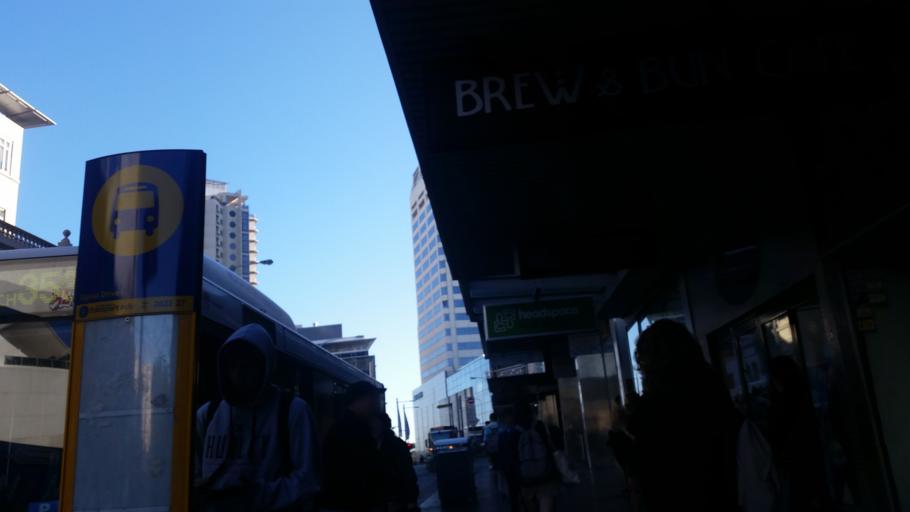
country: AU
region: New South Wales
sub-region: Waverley
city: Bondi Junction
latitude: -33.8932
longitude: 151.2495
